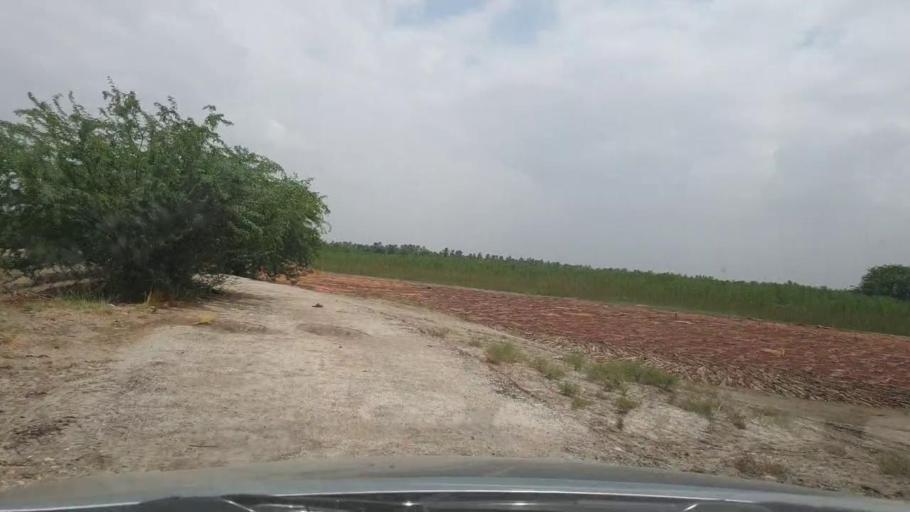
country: PK
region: Sindh
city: Kot Diji
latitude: 27.4274
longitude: 68.7596
